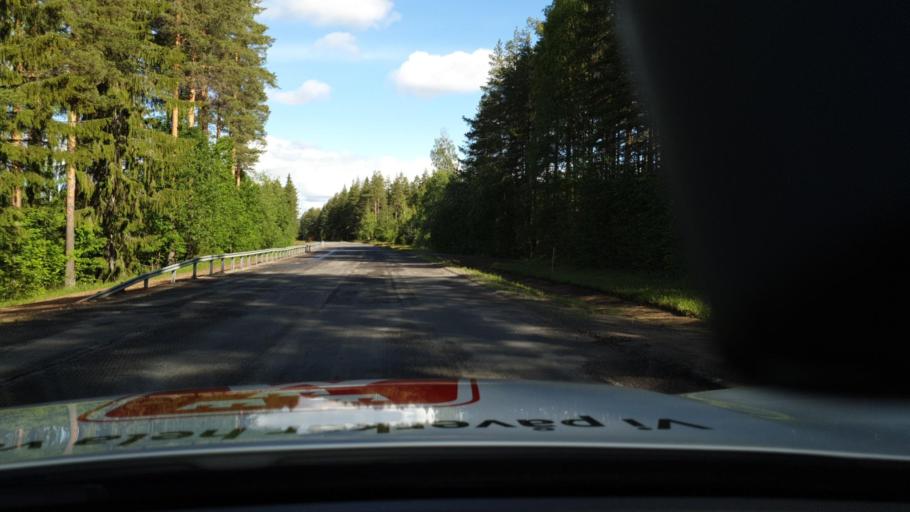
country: SE
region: Norrbotten
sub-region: Bodens Kommun
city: Boden
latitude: 65.8752
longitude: 21.4096
